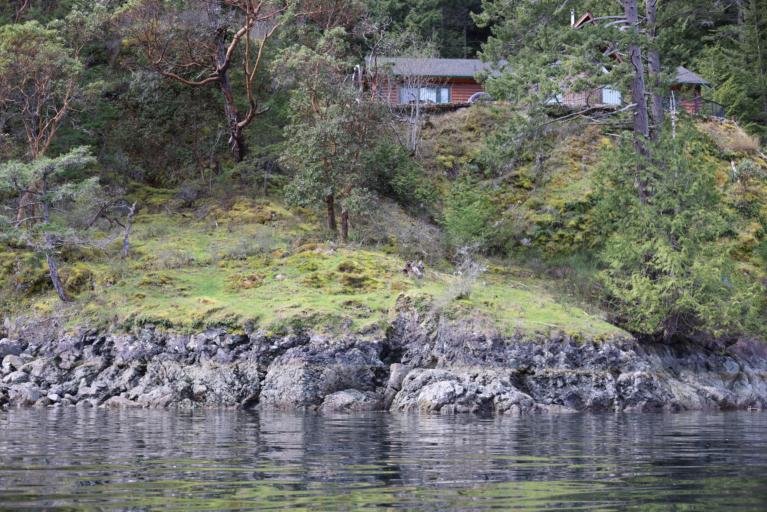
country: CA
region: British Columbia
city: Langford
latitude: 48.5209
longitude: -123.5428
